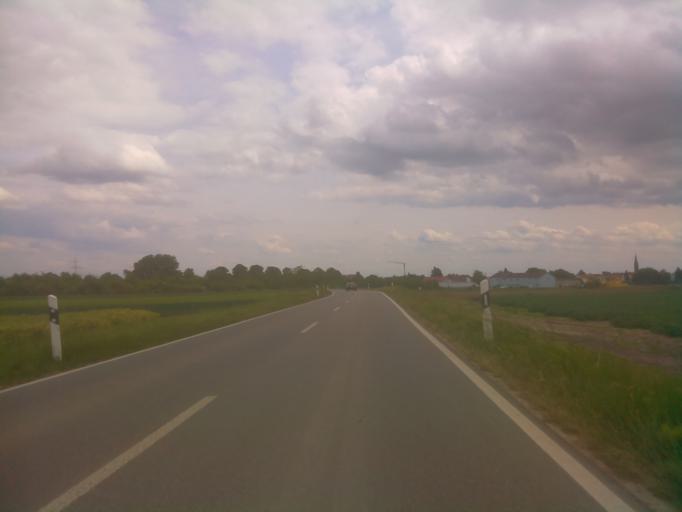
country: DE
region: Rheinland-Pfalz
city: Lambsheim
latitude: 49.5241
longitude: 8.2834
